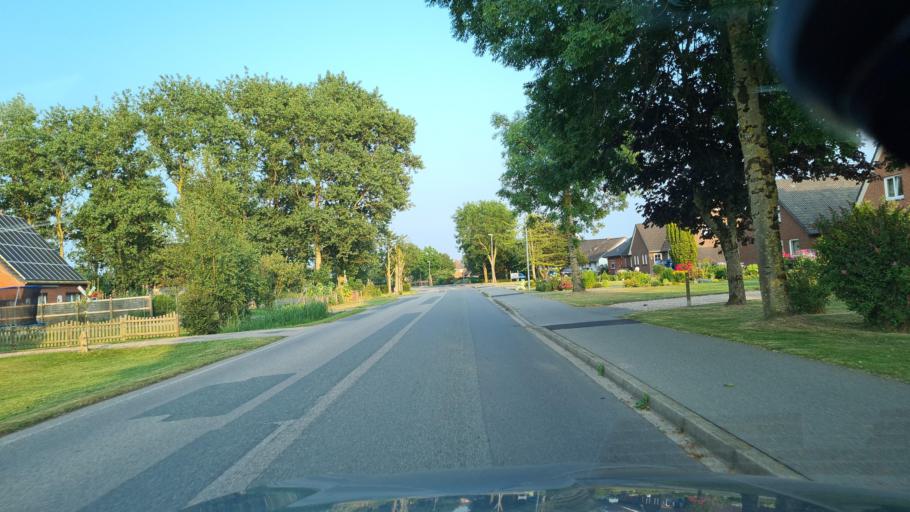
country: DE
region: Schleswig-Holstein
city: Elisabeth-Sophien-Koog
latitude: 54.4911
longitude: 8.8699
